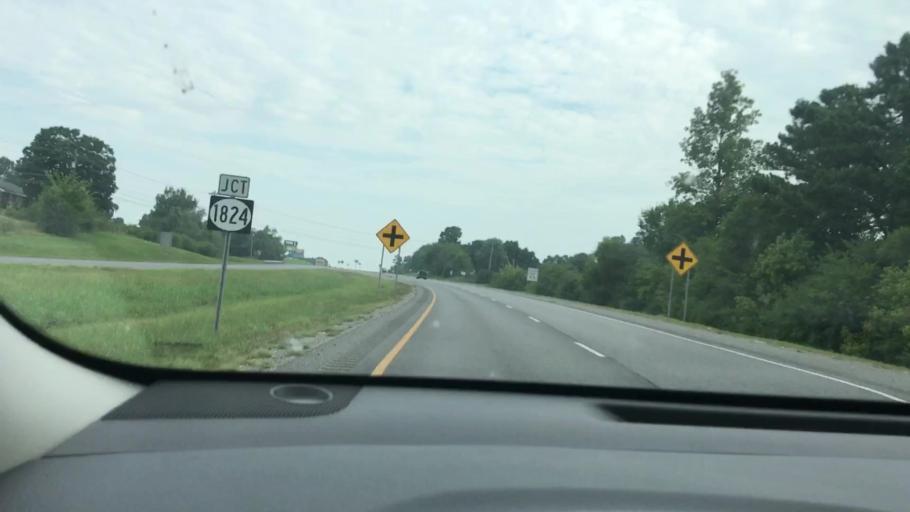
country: US
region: Kentucky
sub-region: Calloway County
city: Murray
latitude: 36.6743
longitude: -88.3025
